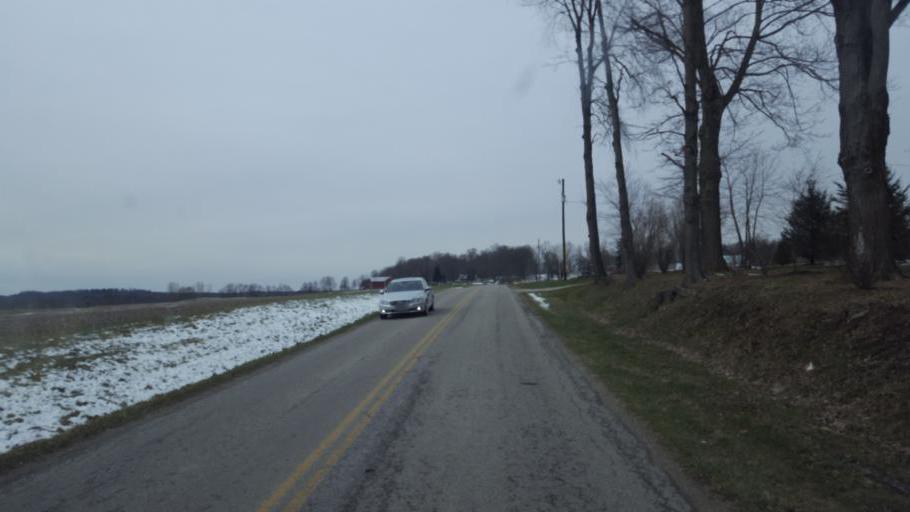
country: US
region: Ohio
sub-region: Richland County
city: Lexington
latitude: 40.7016
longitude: -82.5851
